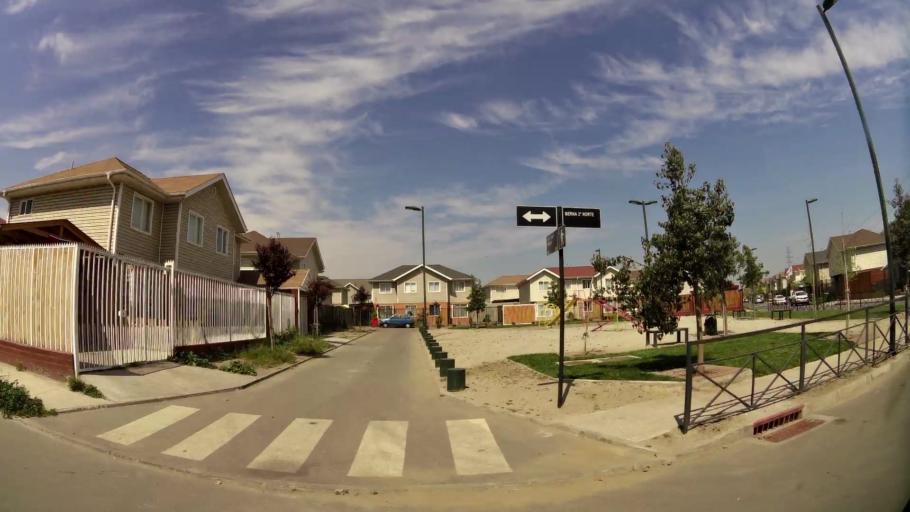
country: CL
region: Santiago Metropolitan
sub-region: Provincia de Cordillera
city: Puente Alto
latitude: -33.5912
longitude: -70.5978
